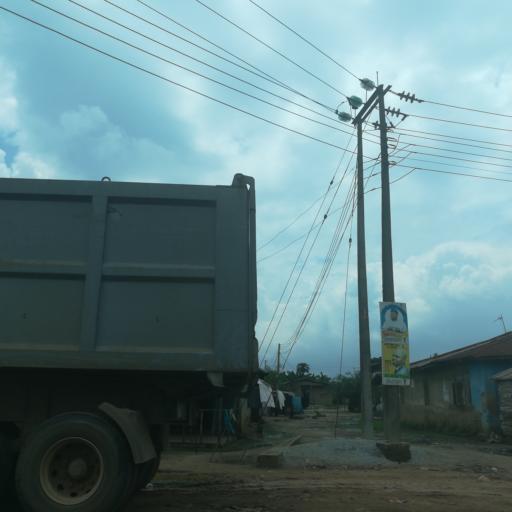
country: NG
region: Lagos
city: Ejirin
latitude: 6.6582
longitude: 3.7947
